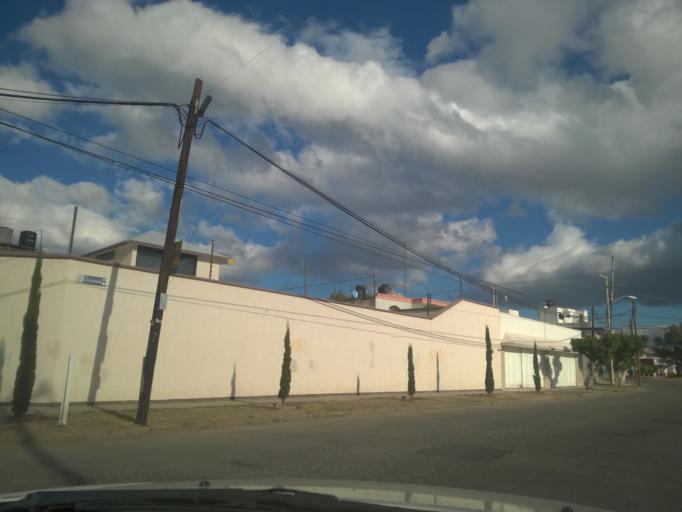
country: MX
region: Guanajuato
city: Leon
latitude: 21.1168
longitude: -101.6498
